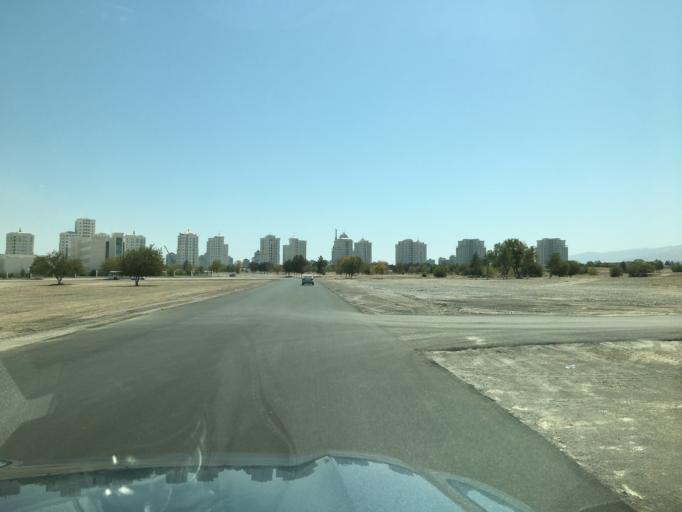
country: TM
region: Ahal
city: Ashgabat
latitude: 37.8904
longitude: 58.3668
